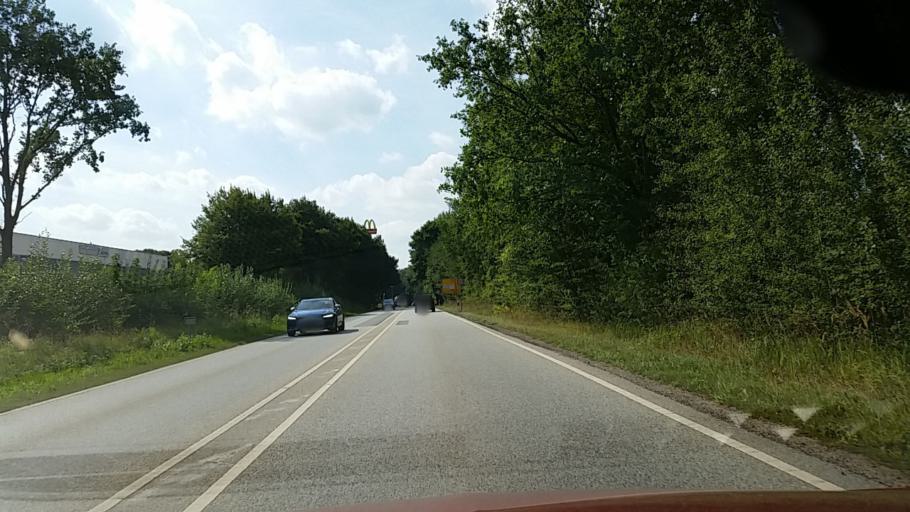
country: DE
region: Schleswig-Holstein
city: Reinbek
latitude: 53.5264
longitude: 10.2282
